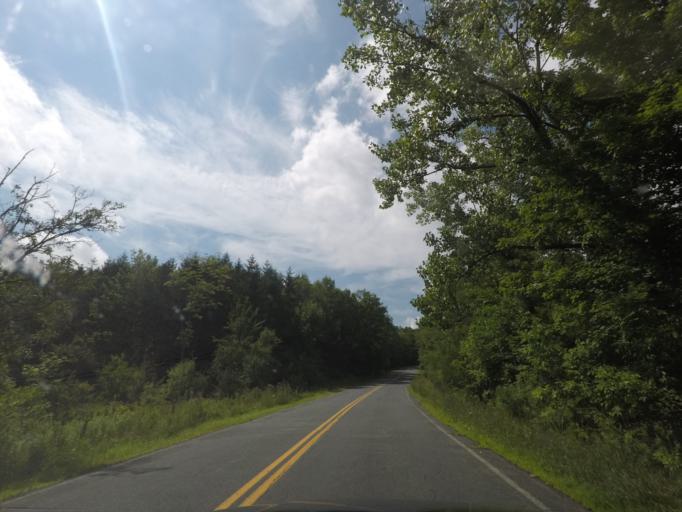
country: US
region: New York
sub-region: Rensselaer County
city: Averill Park
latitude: 42.6012
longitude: -73.5491
